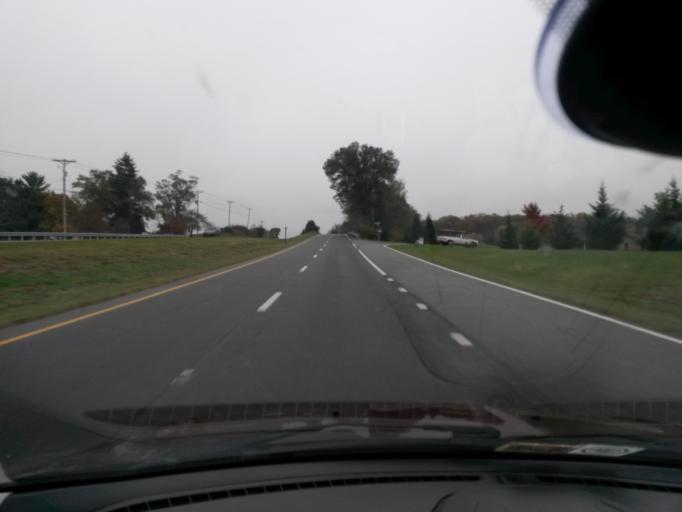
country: US
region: Virginia
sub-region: Botetourt County
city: Daleville
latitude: 37.4479
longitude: -79.9011
